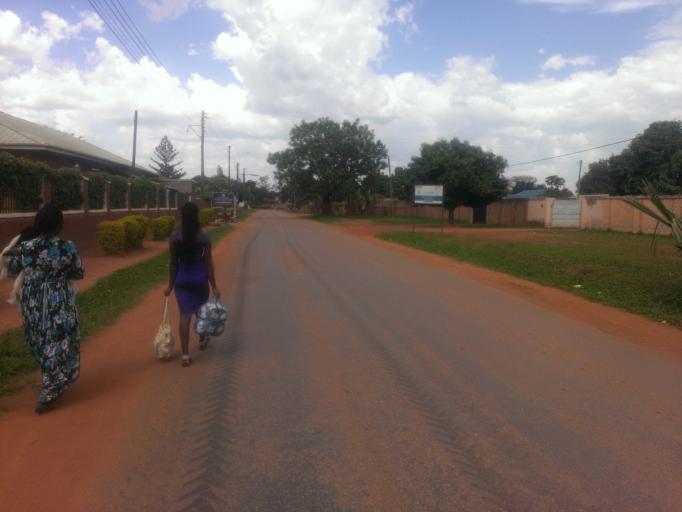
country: UG
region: Northern Region
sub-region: Gulu District
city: Gulu
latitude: 2.7825
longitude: 32.3013
